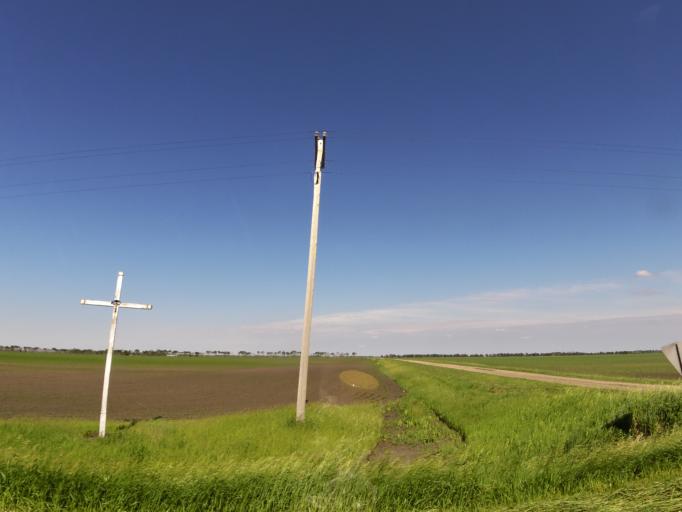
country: US
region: North Dakota
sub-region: Walsh County
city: Grafton
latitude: 48.3100
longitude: -97.2551
